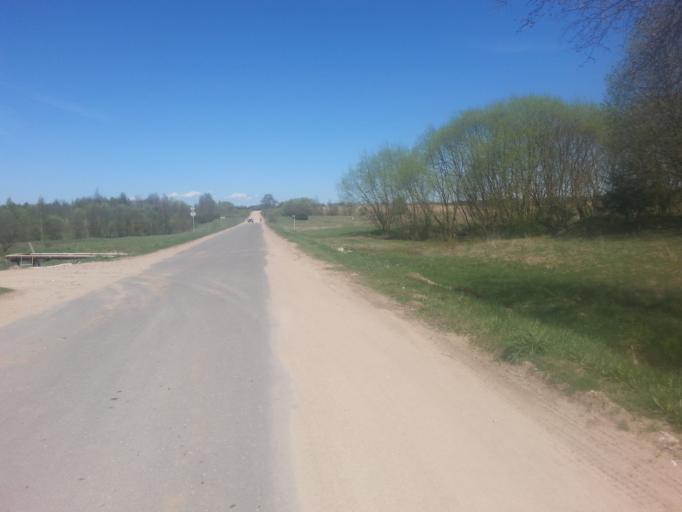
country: BY
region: Minsk
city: Narach
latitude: 54.9450
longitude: 26.6959
